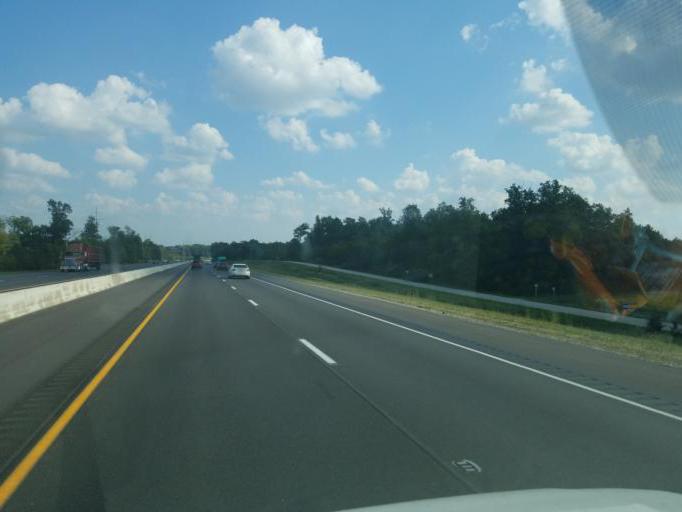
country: US
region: Indiana
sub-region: Allen County
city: Fort Wayne
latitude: 41.1680
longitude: -85.0917
